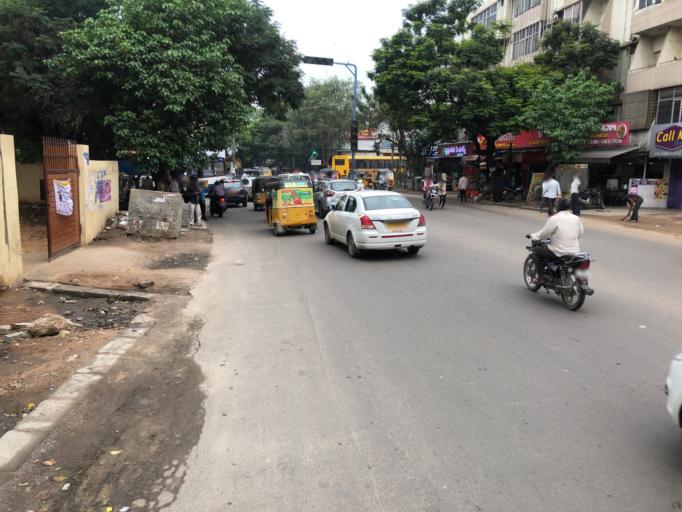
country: IN
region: Telangana
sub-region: Rangareddi
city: Kukatpalli
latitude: 17.4366
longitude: 78.4286
